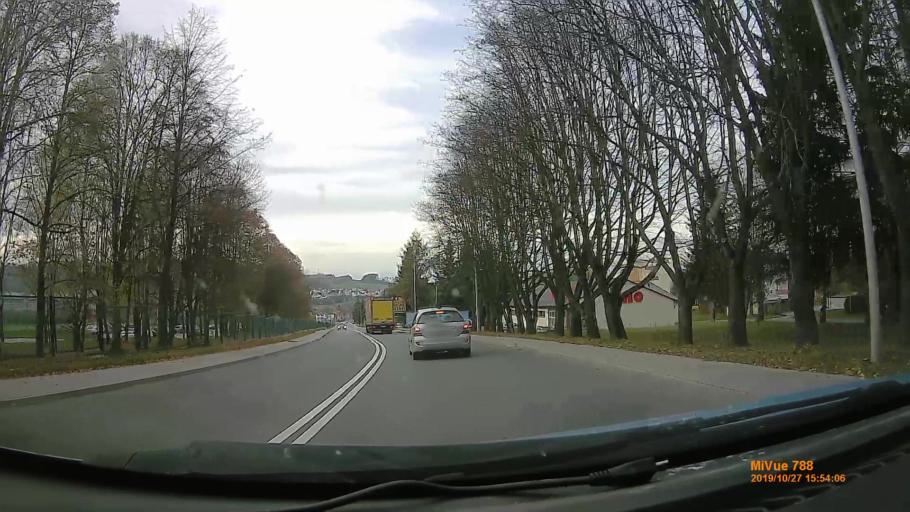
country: PL
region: Lower Silesian Voivodeship
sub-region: Powiat klodzki
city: Bozkow
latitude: 50.5409
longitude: 16.5609
